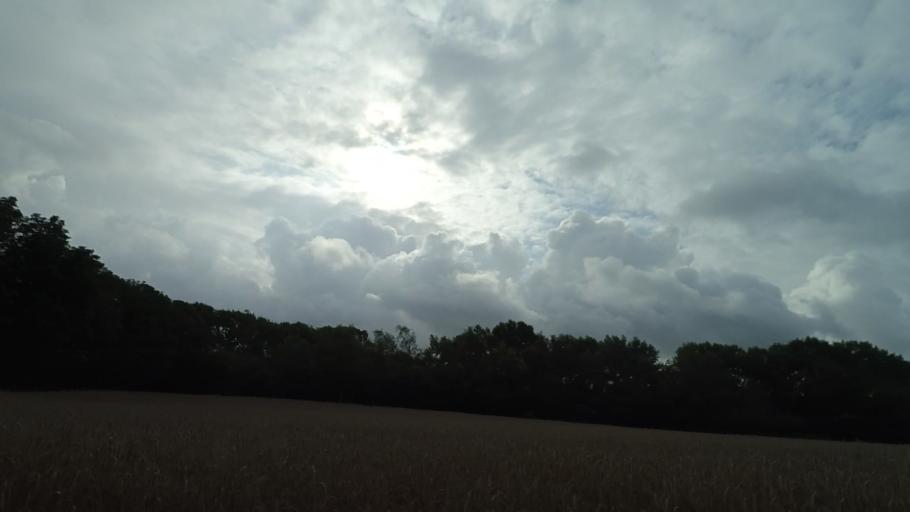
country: DK
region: Central Jutland
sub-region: Syddjurs Kommune
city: Ronde
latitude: 56.3419
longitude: 10.4870
